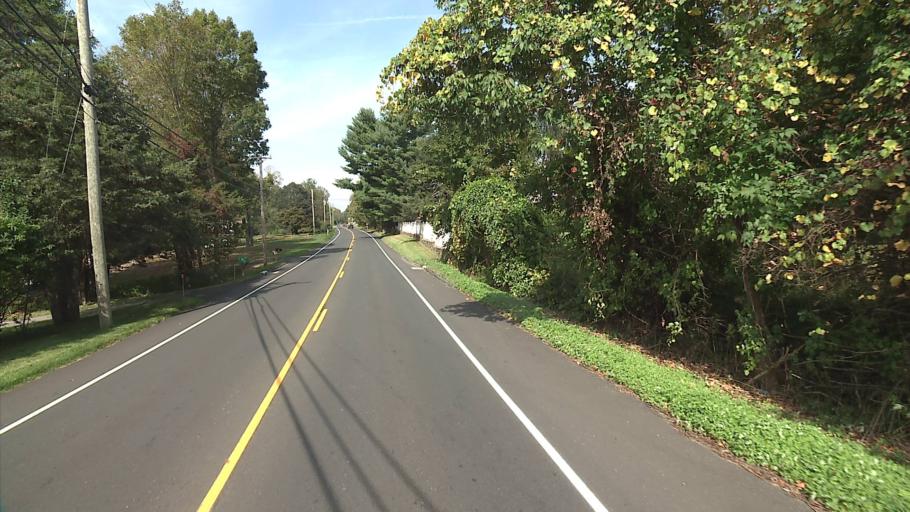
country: US
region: Connecticut
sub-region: Fairfield County
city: Newtown
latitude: 41.4037
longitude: -73.2505
